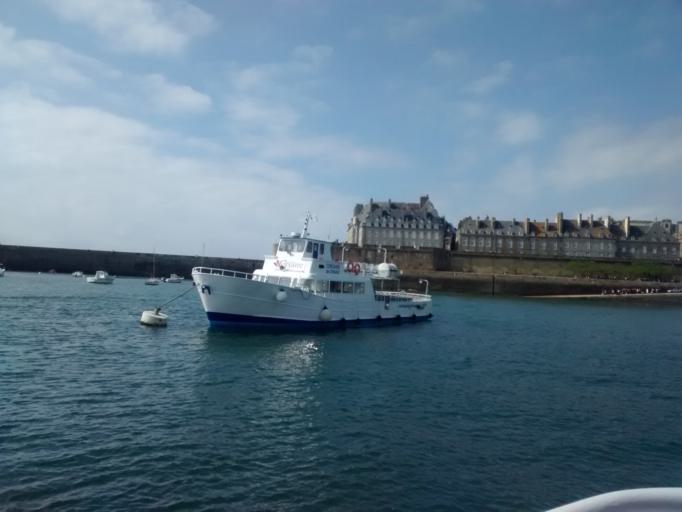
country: FR
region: Brittany
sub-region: Departement d'Ille-et-Vilaine
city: Saint-Malo
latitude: 48.6438
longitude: -2.0267
